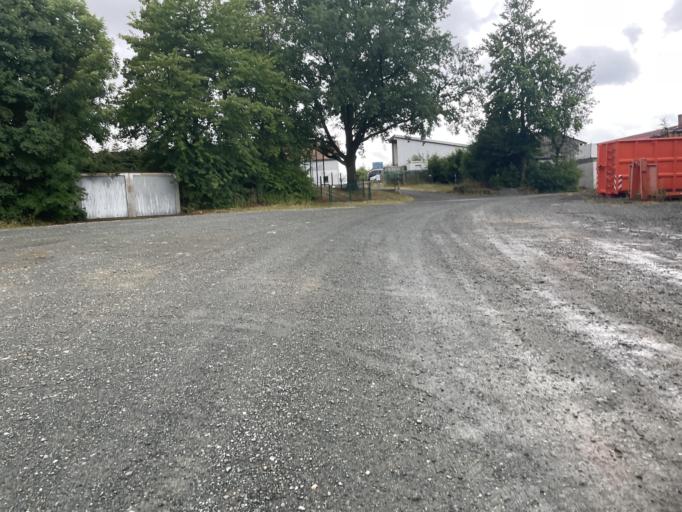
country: DE
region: Bavaria
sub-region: Upper Franconia
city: Neunkirchen am Main
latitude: 49.9404
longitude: 11.6424
